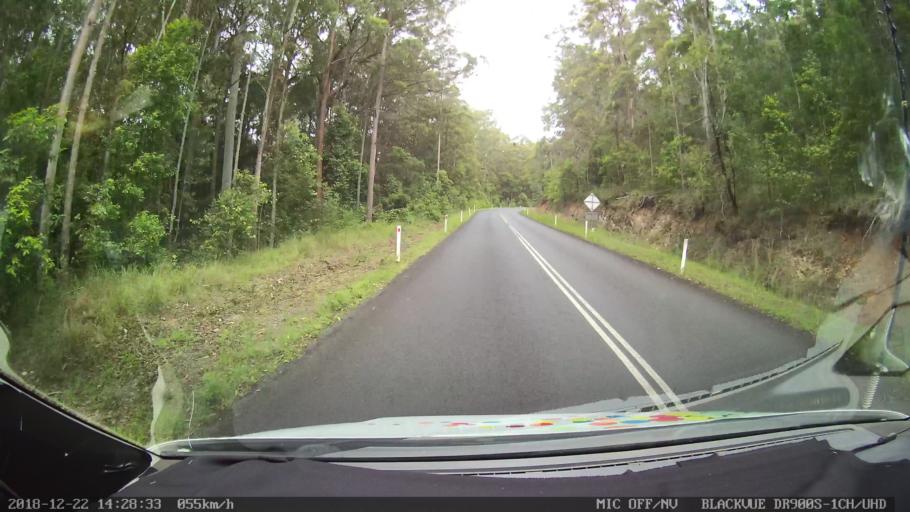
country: AU
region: New South Wales
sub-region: Bellingen
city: Dorrigo
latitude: -30.0737
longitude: 152.6367
